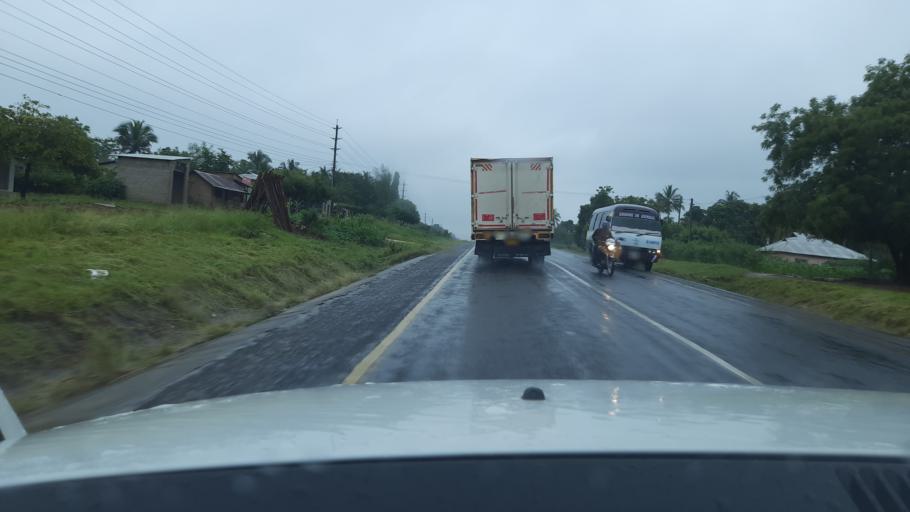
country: TZ
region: Pwani
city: Bagamoyo
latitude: -6.5846
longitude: 39.0407
